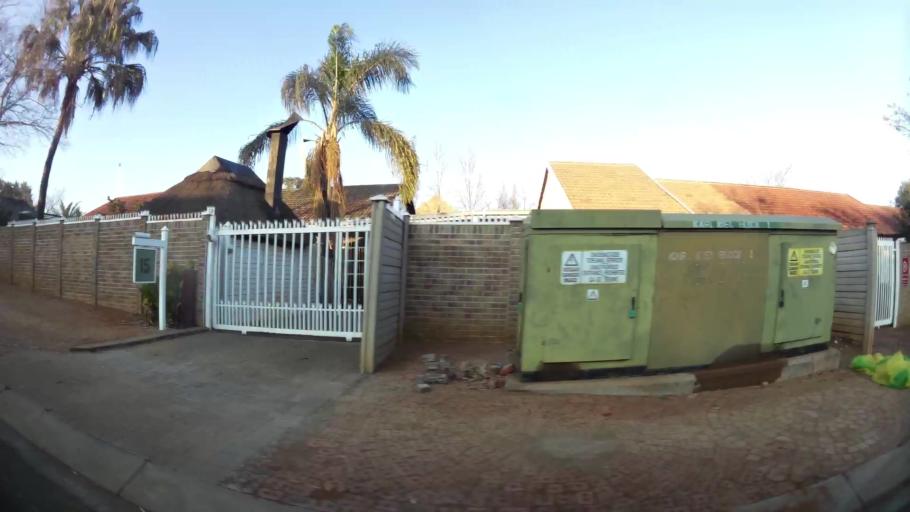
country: ZA
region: Orange Free State
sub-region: Mangaung Metropolitan Municipality
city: Bloemfontein
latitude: -29.0846
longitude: 26.1605
